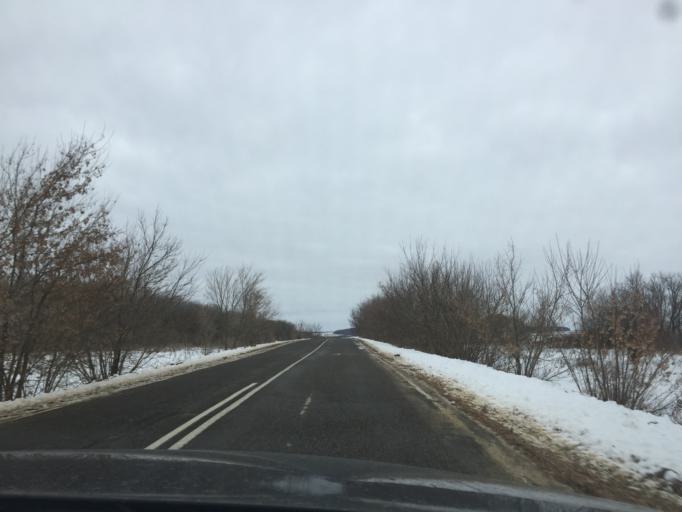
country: RU
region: Tula
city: Teploye
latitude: 53.7863
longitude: 37.6195
